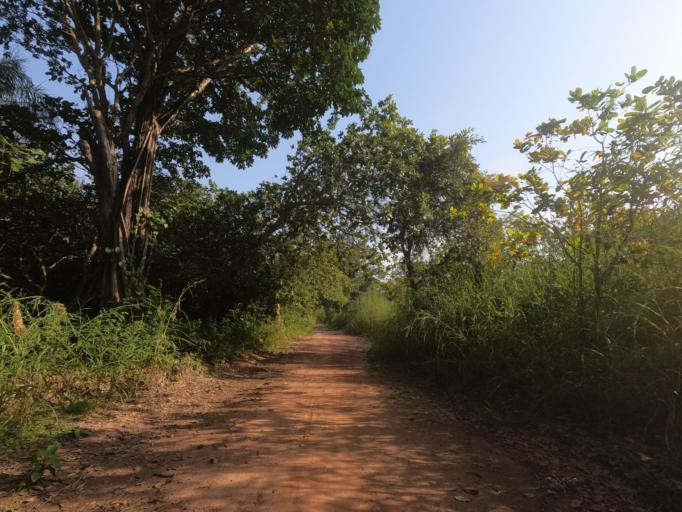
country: GW
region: Oio
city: Bissora
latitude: 12.4109
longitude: -15.7301
